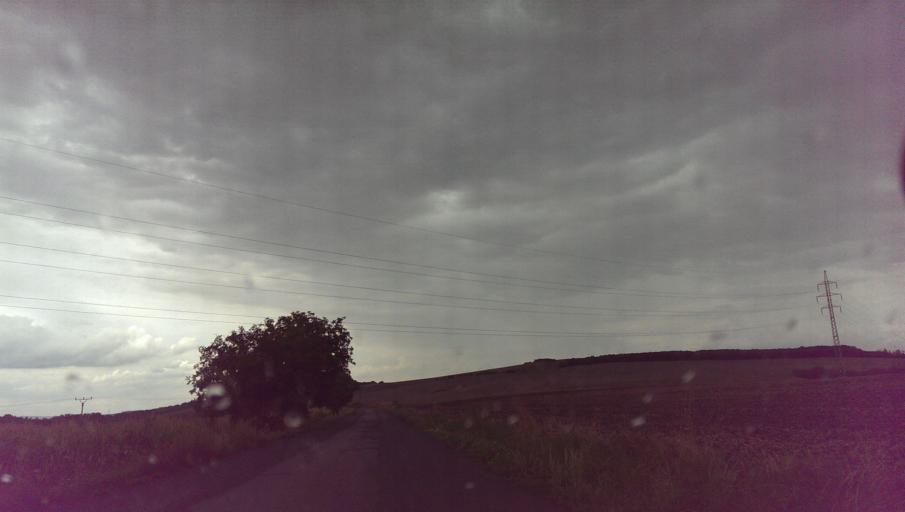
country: CZ
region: Zlin
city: Dolni Nemci
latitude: 48.9409
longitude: 17.5710
